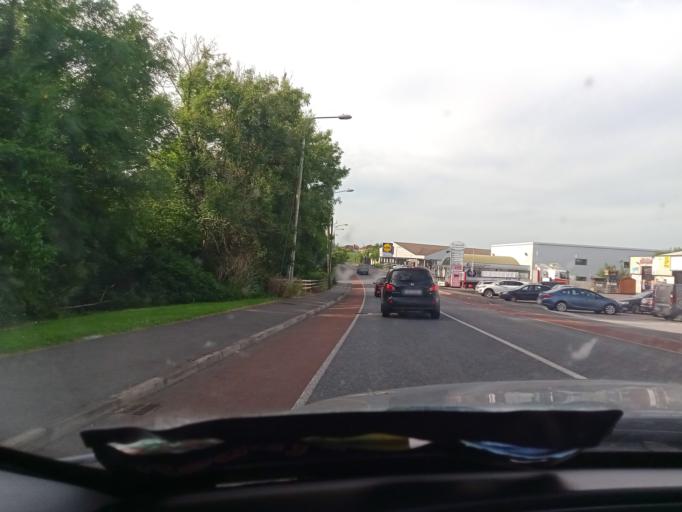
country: IE
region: Ulster
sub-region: An Cabhan
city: Cavan
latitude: 53.9752
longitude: -7.3544
